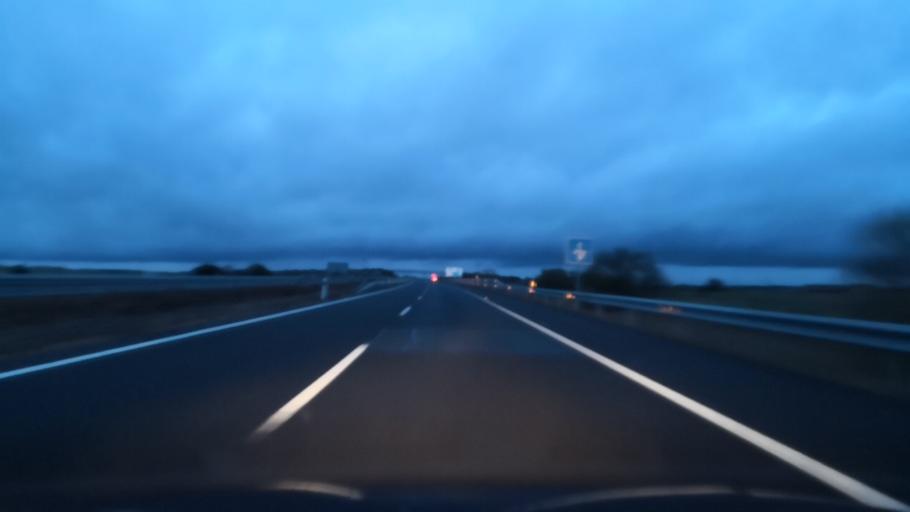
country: ES
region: Extremadura
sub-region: Provincia de Caceres
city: Aldea del Cano
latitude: 39.2792
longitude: -6.3252
